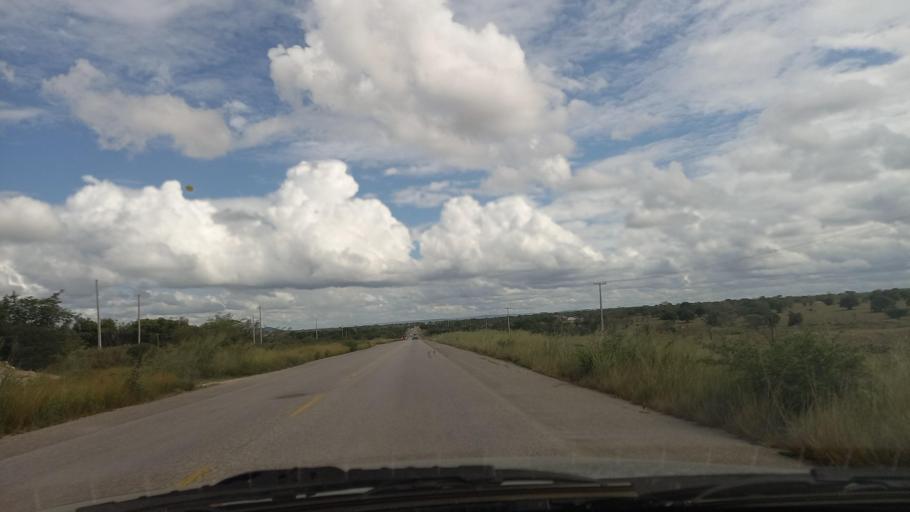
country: BR
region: Pernambuco
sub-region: Cachoeirinha
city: Cachoeirinha
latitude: -8.4222
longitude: -36.1953
